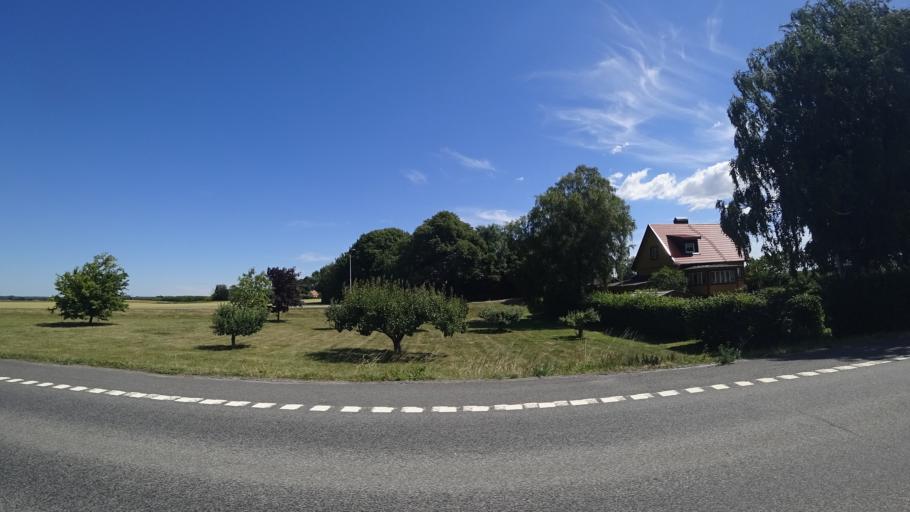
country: SE
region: Skane
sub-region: Kristianstads Kommun
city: Kristianstad
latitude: 56.0276
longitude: 14.1013
